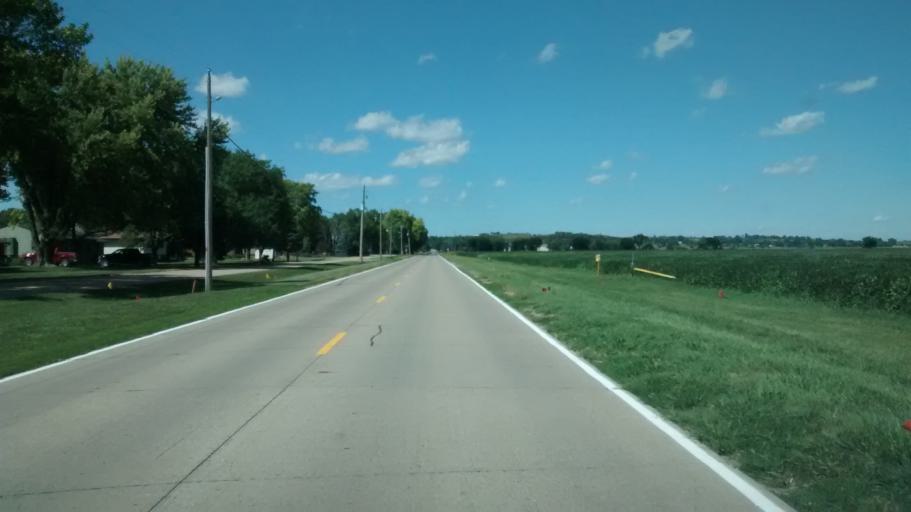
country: US
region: Iowa
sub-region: Woodbury County
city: Sergeant Bluff
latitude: 42.3904
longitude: -96.3407
